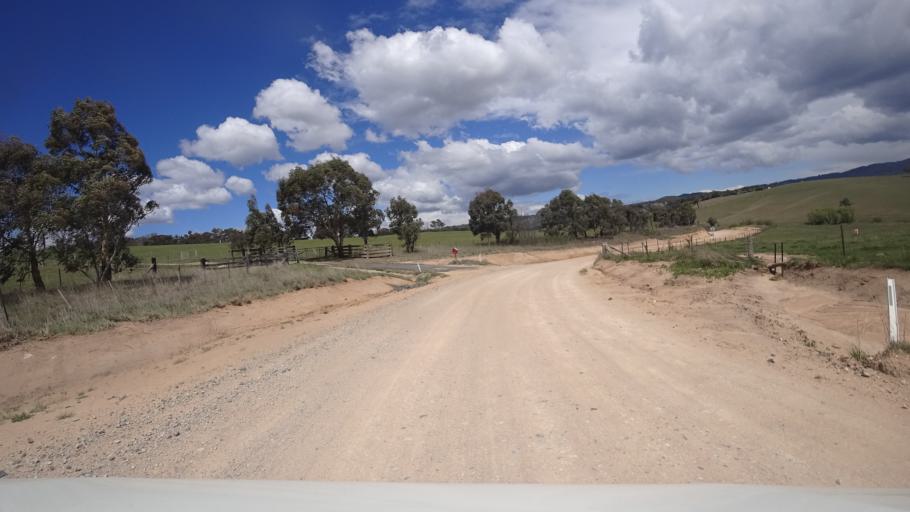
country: AU
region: New South Wales
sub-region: Oberon
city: Oberon
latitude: -33.5758
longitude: 149.8972
